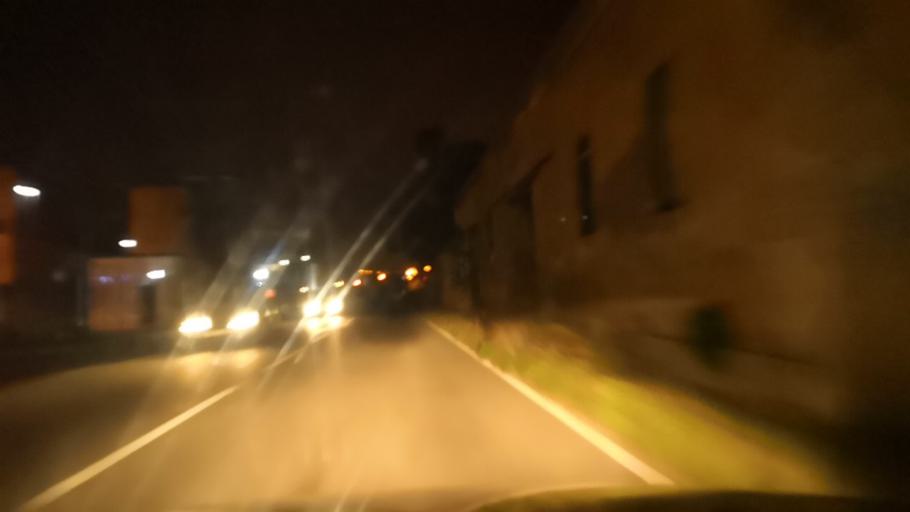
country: PT
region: Setubal
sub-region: Setubal
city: Setubal
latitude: 38.5114
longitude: -8.8556
